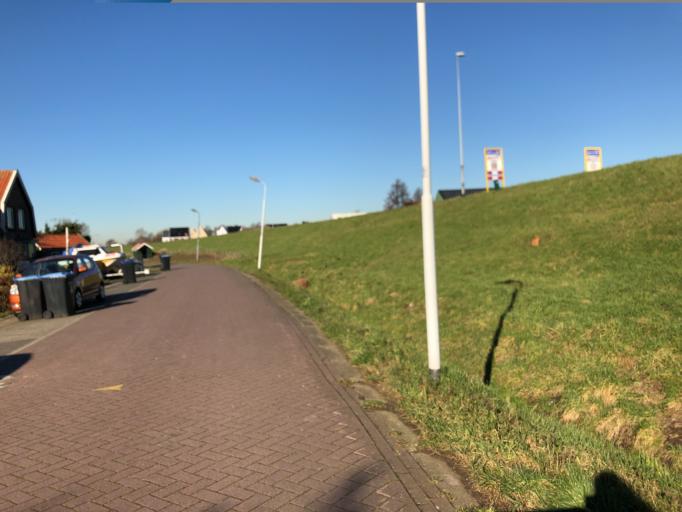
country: NL
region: North Holland
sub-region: Gemeente Zaanstad
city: Zaanstad
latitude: 52.4325
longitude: 4.7794
